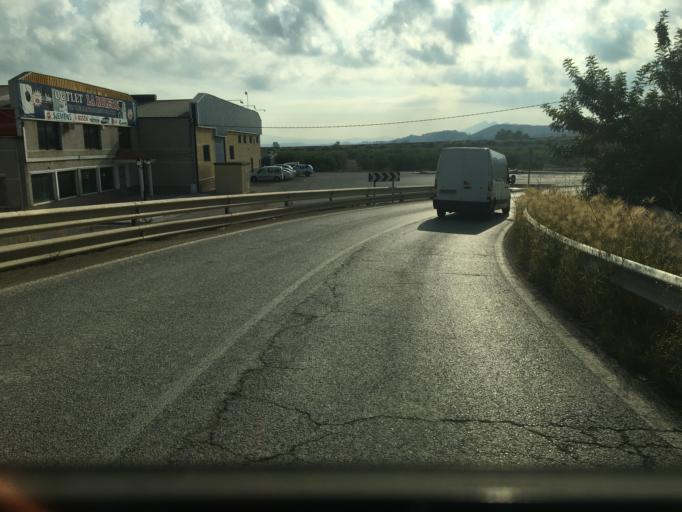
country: ES
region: Murcia
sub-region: Murcia
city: Beniel
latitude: 38.0021
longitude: -1.0205
